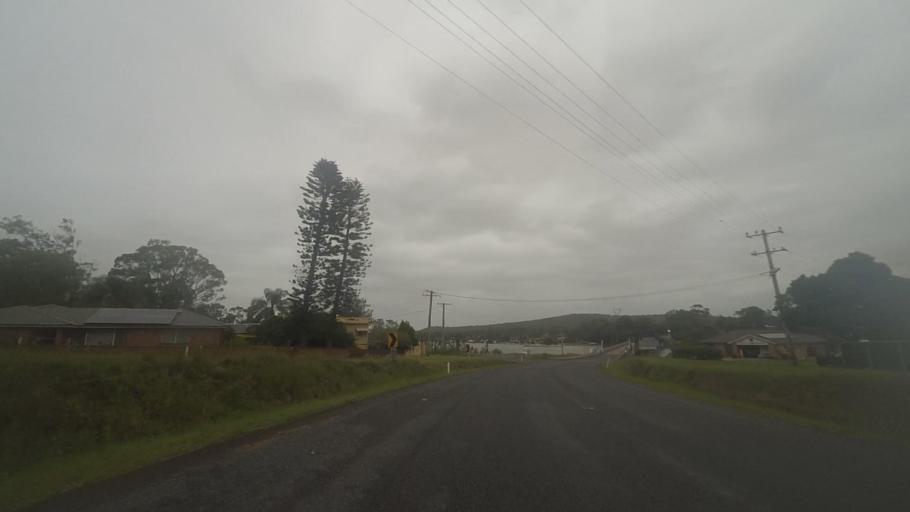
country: AU
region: New South Wales
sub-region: Port Stephens Shire
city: Port Stephens
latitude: -32.6530
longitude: 151.9713
